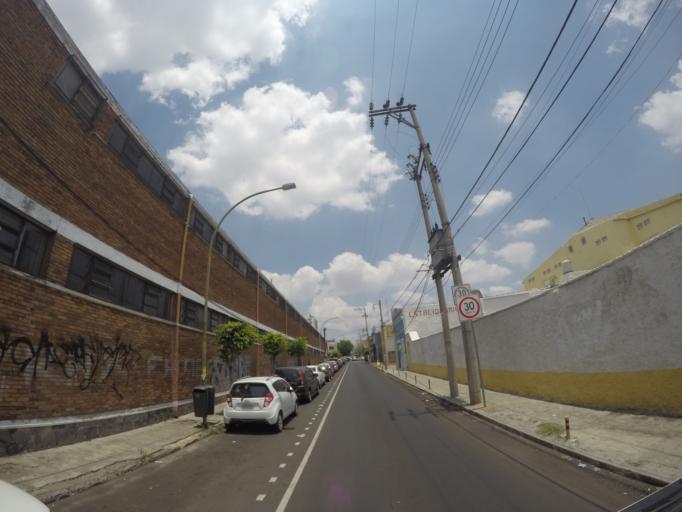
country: MX
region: Jalisco
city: Guadalajara
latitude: 20.6828
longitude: -103.3572
